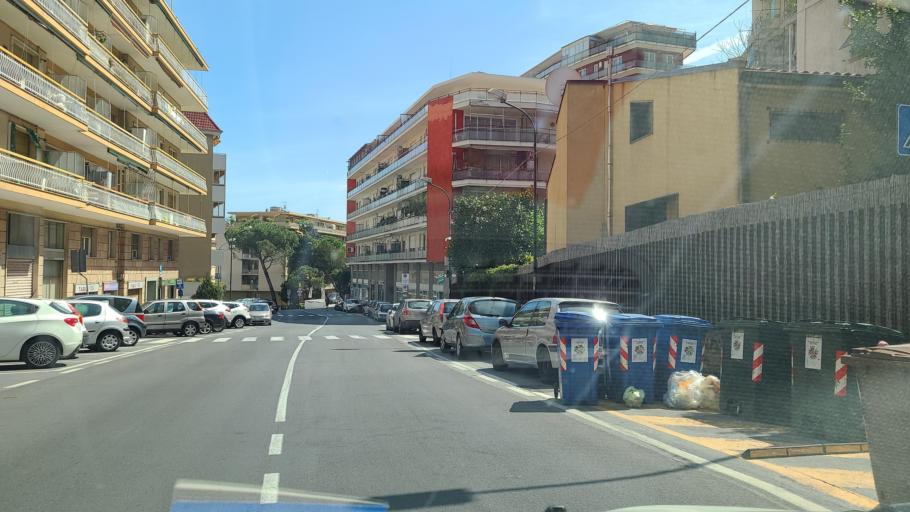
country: IT
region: Liguria
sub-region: Provincia di Imperia
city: San Remo
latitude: 43.8214
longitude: 7.7675
